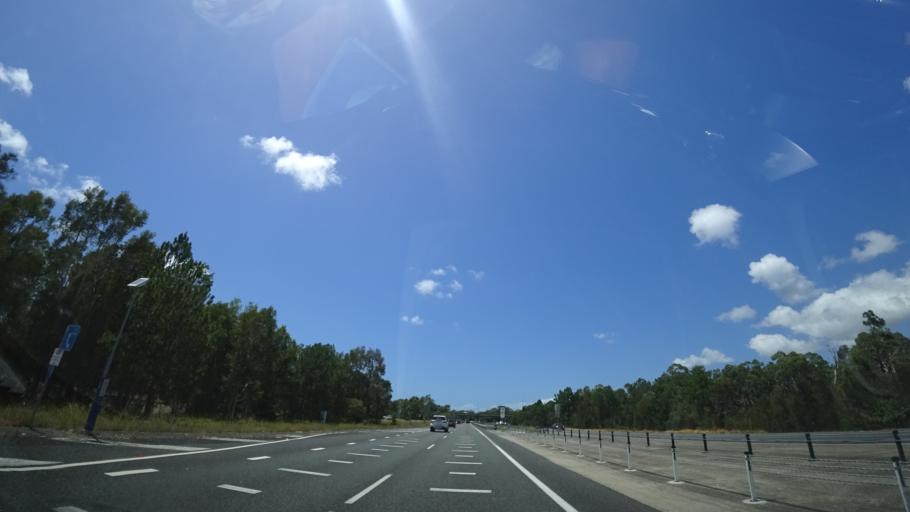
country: AU
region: Queensland
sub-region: Sunshine Coast
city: Mooloolaba
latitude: -26.6913
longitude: 153.1097
